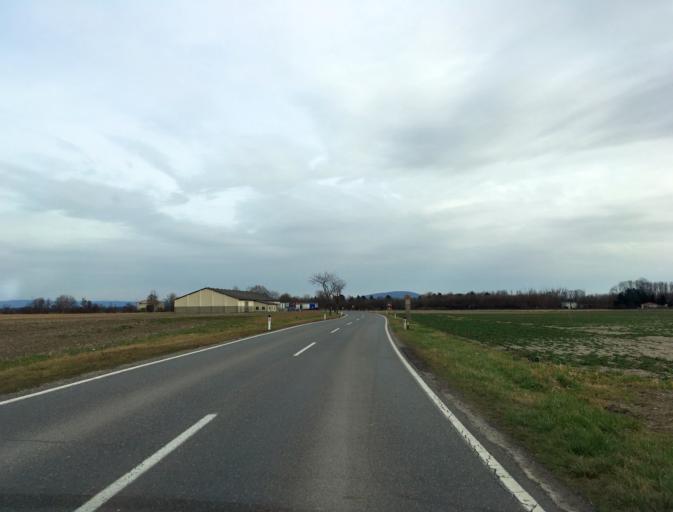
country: AT
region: Lower Austria
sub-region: Politischer Bezirk Ganserndorf
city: Lassee
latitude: 48.2248
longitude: 16.8364
